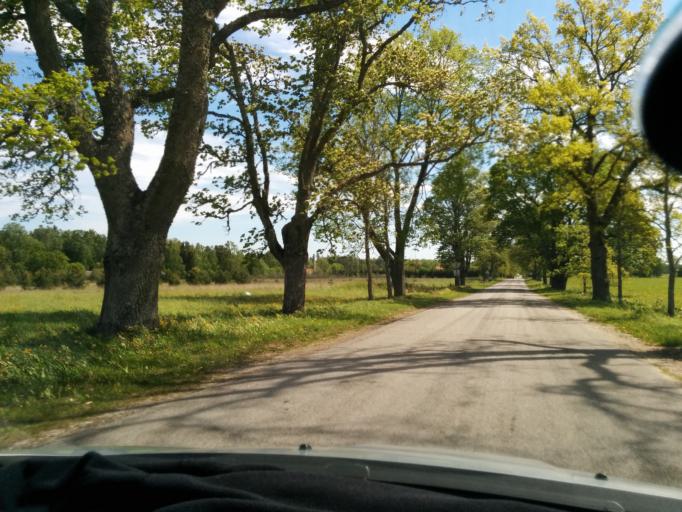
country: EE
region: Harju
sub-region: Loksa linn
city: Loksa
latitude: 59.5161
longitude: 25.9456
